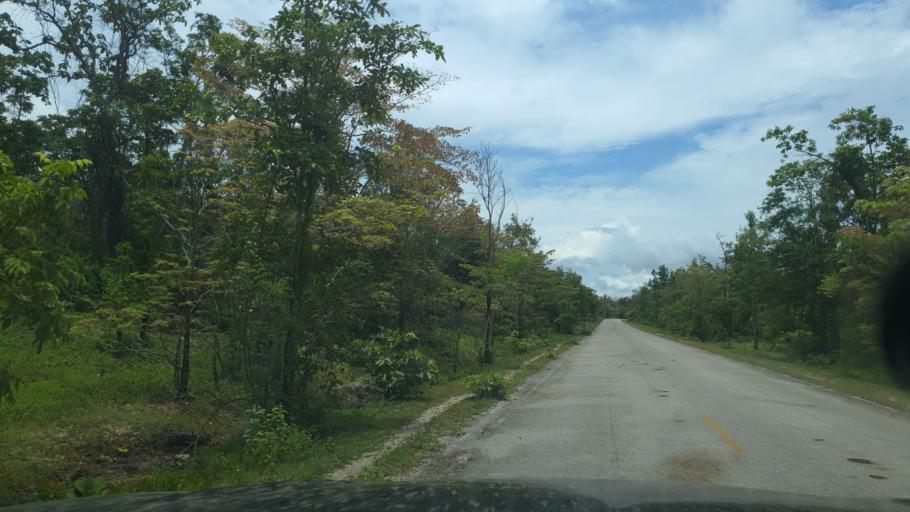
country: TH
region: Lampang
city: Soem Ngam
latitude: 18.0547
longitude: 99.3620
